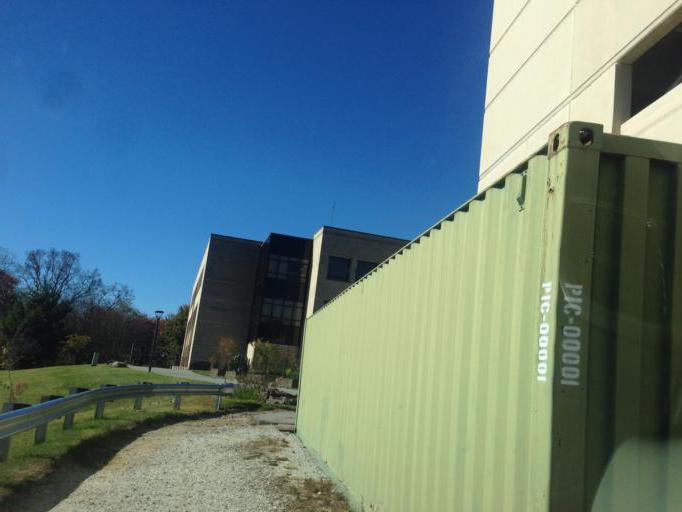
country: US
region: Maryland
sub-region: Howard County
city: Riverside
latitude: 39.2128
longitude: -76.8772
